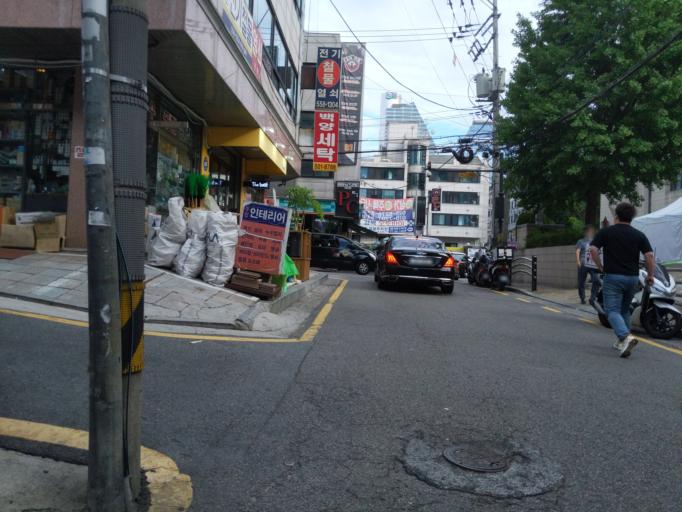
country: KR
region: Seoul
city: Seoul
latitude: 37.5073
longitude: 127.0352
